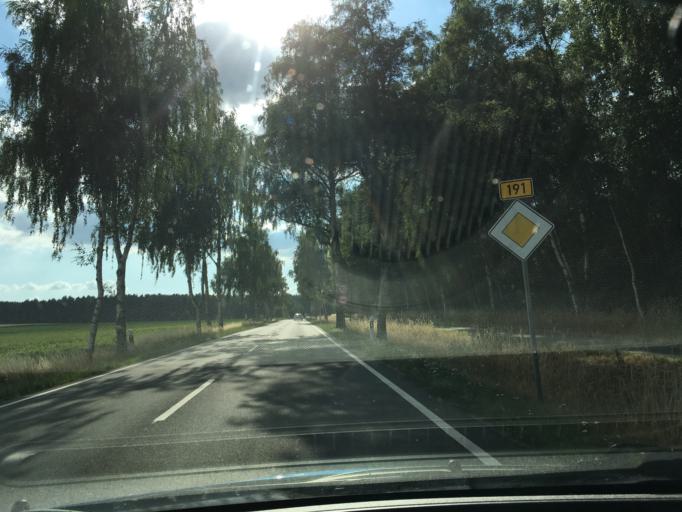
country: DE
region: Lower Saxony
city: Karwitz
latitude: 53.0833
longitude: 11.0060
